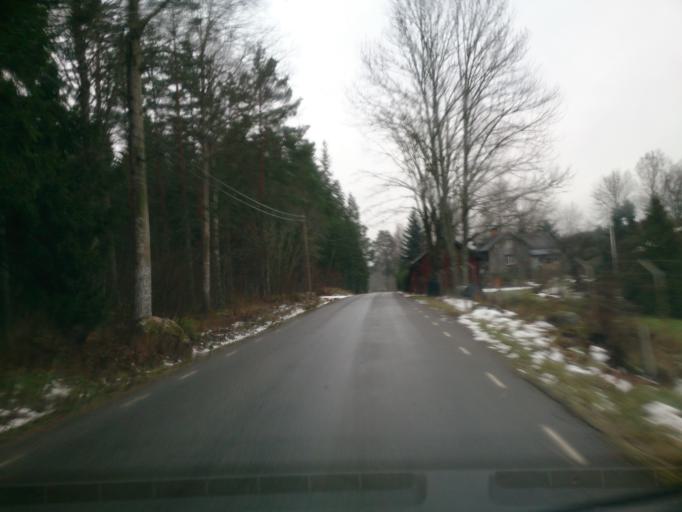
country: SE
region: OEstergoetland
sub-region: Atvidabergs Kommun
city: Atvidaberg
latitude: 58.2530
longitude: 16.1016
